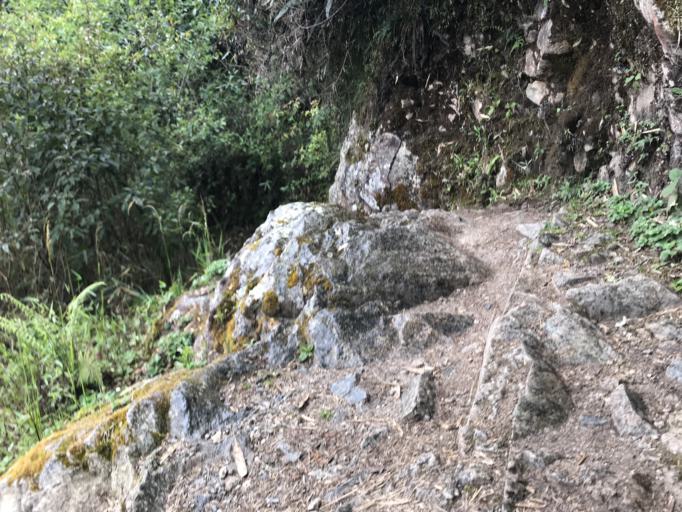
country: PE
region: Cusco
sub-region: Provincia de La Convencion
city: Santa Teresa
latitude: -13.1741
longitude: -72.5353
